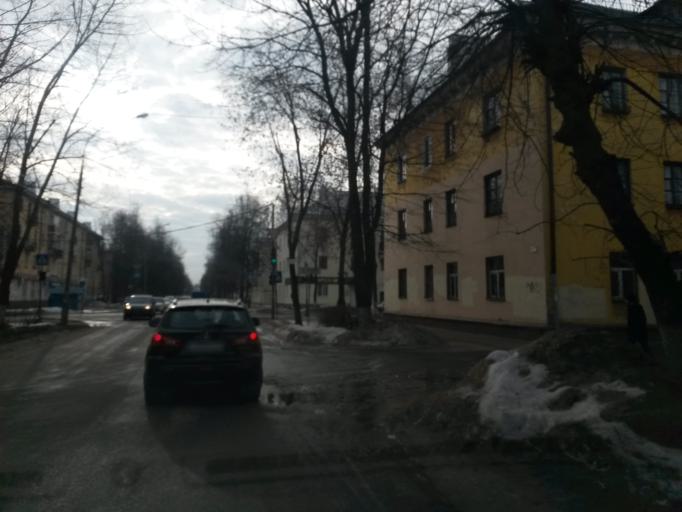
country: RU
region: Jaroslavl
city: Yaroslavl
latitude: 57.6356
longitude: 39.8460
